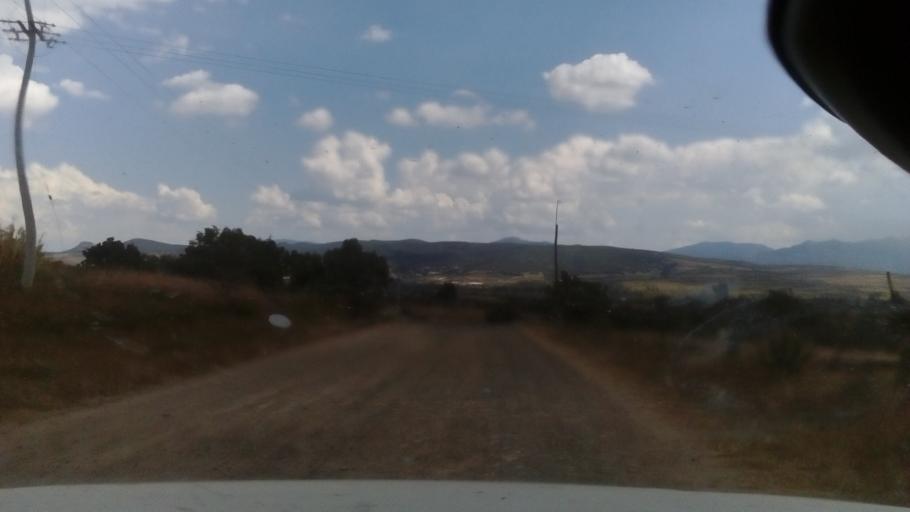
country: MX
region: Guanajuato
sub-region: Silao de la Victoria
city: San Francisco (Banos de Agua Caliente)
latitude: 21.1999
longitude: -101.4487
